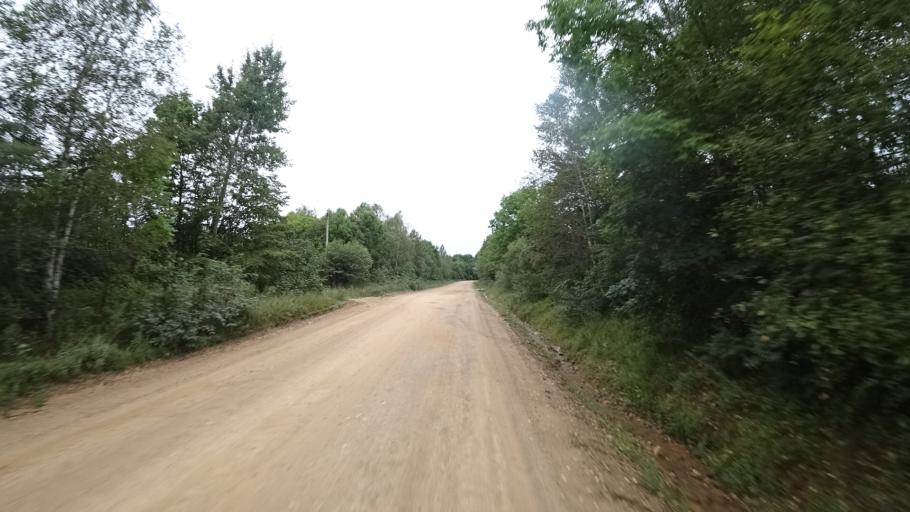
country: RU
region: Primorskiy
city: Rettikhovka
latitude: 44.1811
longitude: 132.8045
